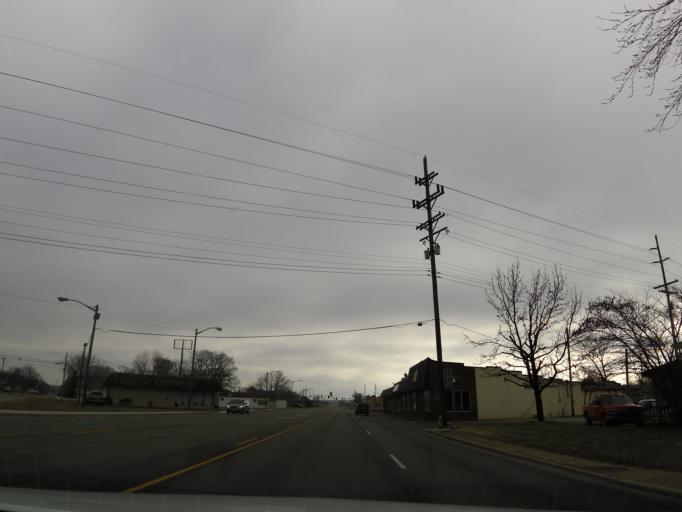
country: US
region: Indiana
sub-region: Bartholomew County
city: Columbus
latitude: 39.1977
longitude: -85.9044
